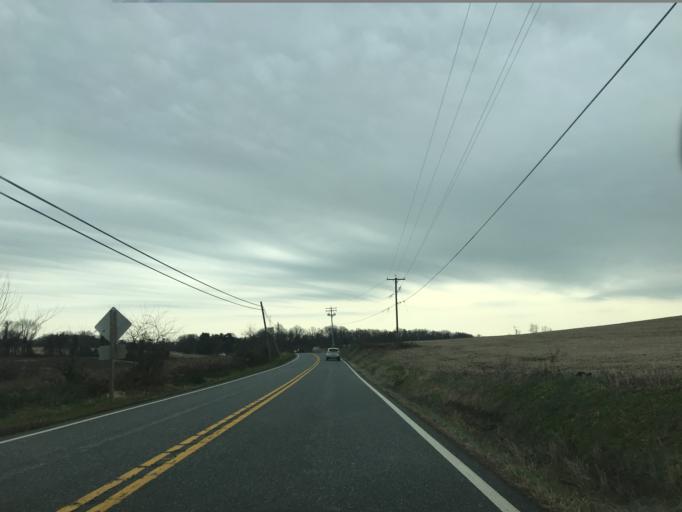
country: US
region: Maryland
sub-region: Harford County
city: Bel Air North
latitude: 39.5950
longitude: -76.3460
